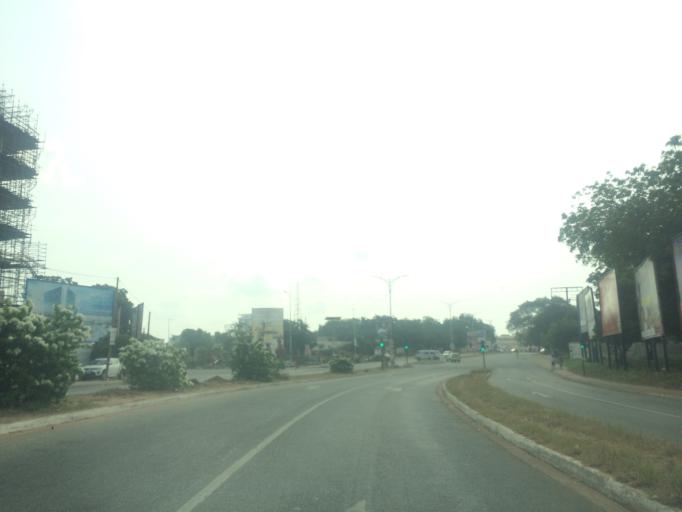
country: GH
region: Greater Accra
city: Accra
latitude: 5.5629
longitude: -0.2028
